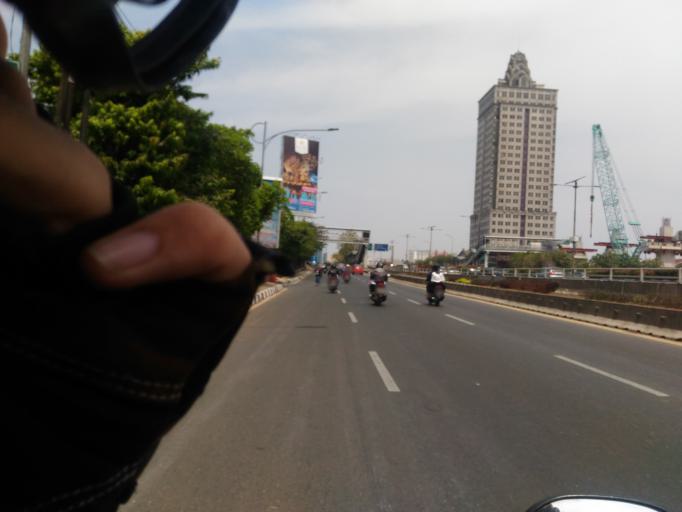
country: ID
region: Jakarta Raya
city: Jakarta
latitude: -6.2430
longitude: 106.8563
